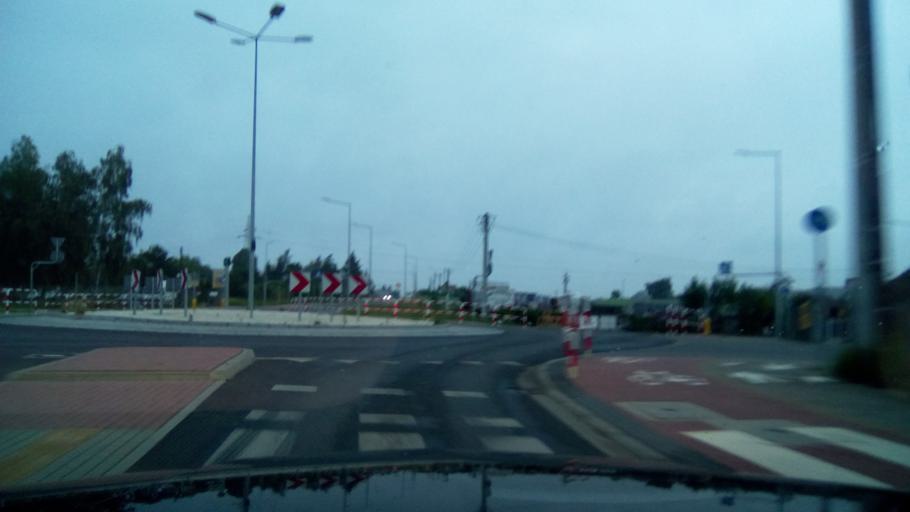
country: PL
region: Greater Poland Voivodeship
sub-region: Powiat poznanski
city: Kobylnica
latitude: 52.4314
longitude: 17.0725
